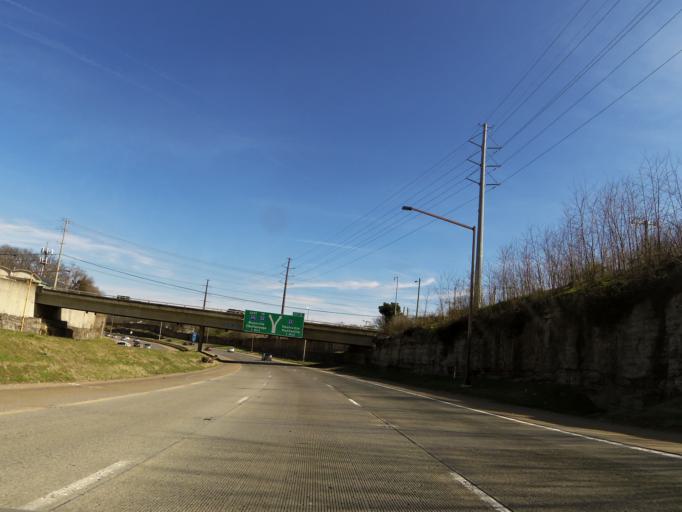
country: US
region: Tennessee
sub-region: Davidson County
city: Oak Hill
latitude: 36.1167
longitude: -86.7994
